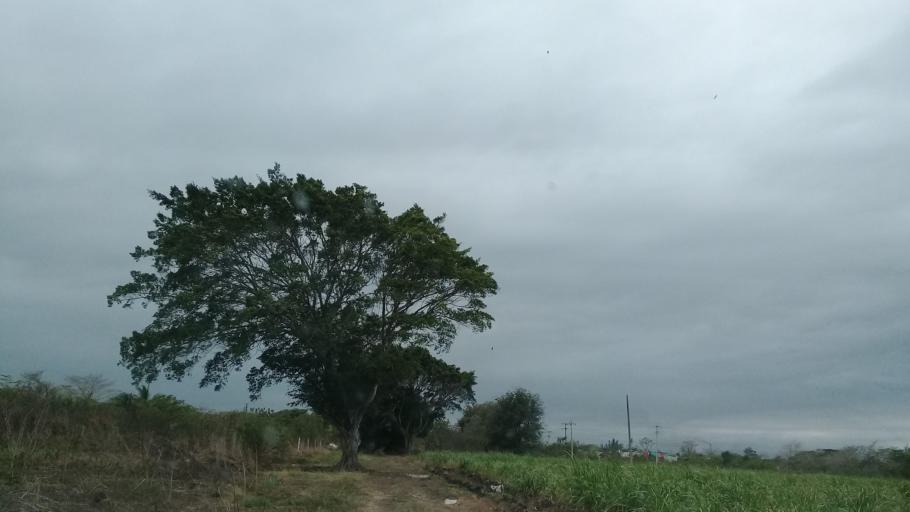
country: MX
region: Veracruz
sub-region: La Antigua
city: Nicolas Blanco (San Pancho)
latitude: 19.3598
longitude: -96.3538
